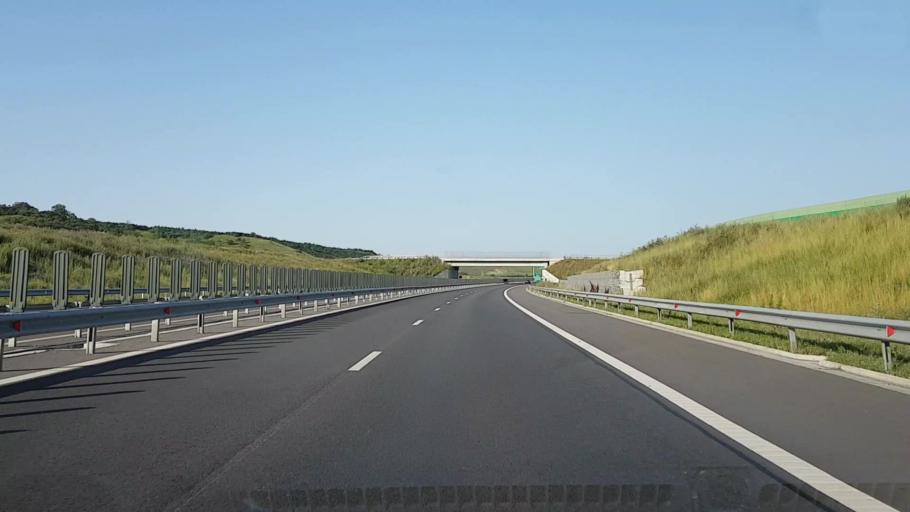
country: RO
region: Alba
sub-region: Comuna Miraslau
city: Miraslau
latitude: 46.3841
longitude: 23.7582
